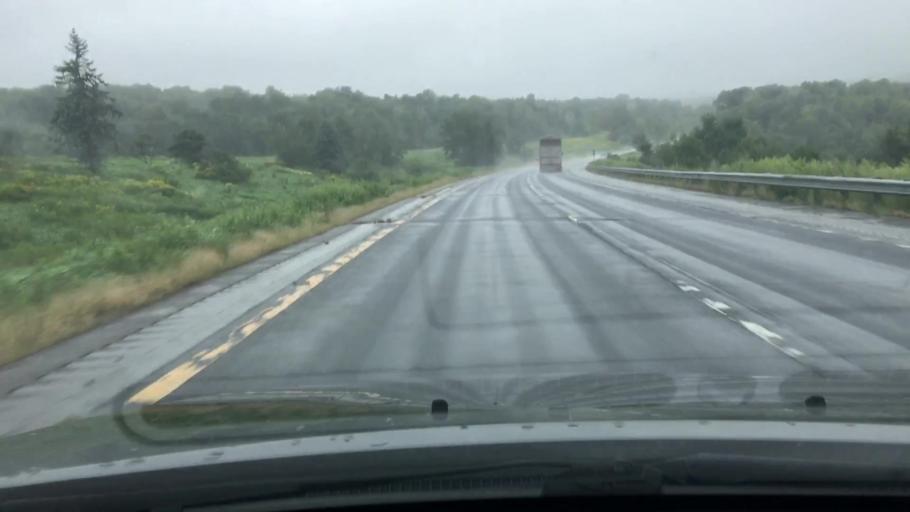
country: US
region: Pennsylvania
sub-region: Lackawanna County
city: Mount Cobb
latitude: 41.3575
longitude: -75.4227
